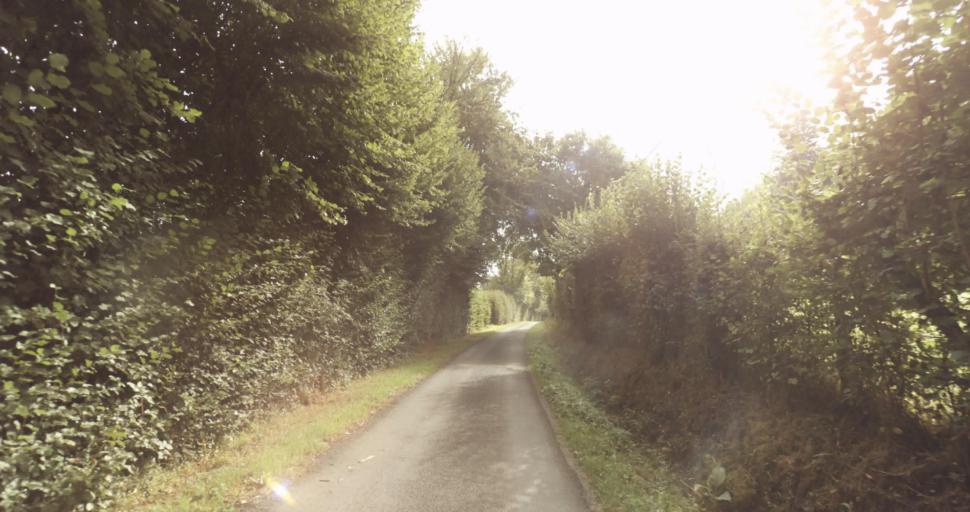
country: FR
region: Lower Normandy
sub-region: Departement de l'Orne
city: Gace
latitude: 48.8385
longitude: 0.3095
